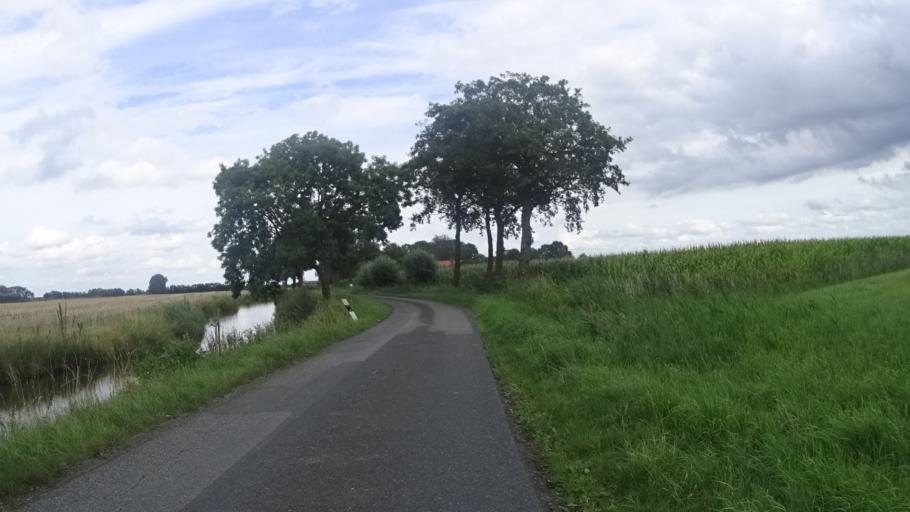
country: DE
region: Lower Saxony
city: Osten
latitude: 53.6963
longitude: 9.2343
